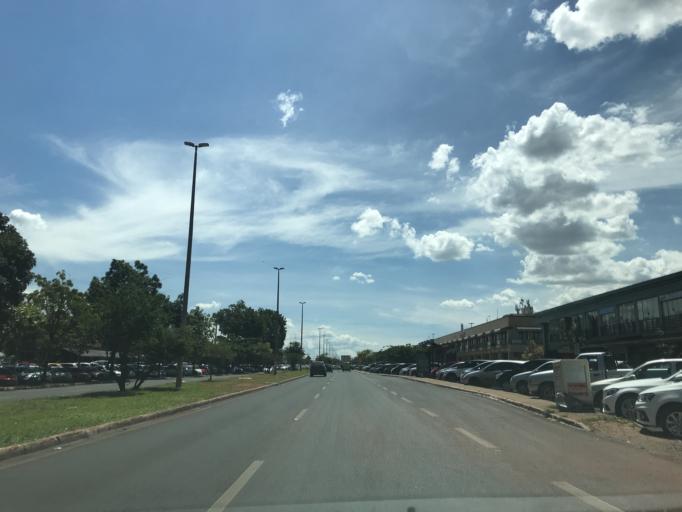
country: BR
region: Federal District
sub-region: Brasilia
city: Brasilia
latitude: -15.7976
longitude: -47.9199
